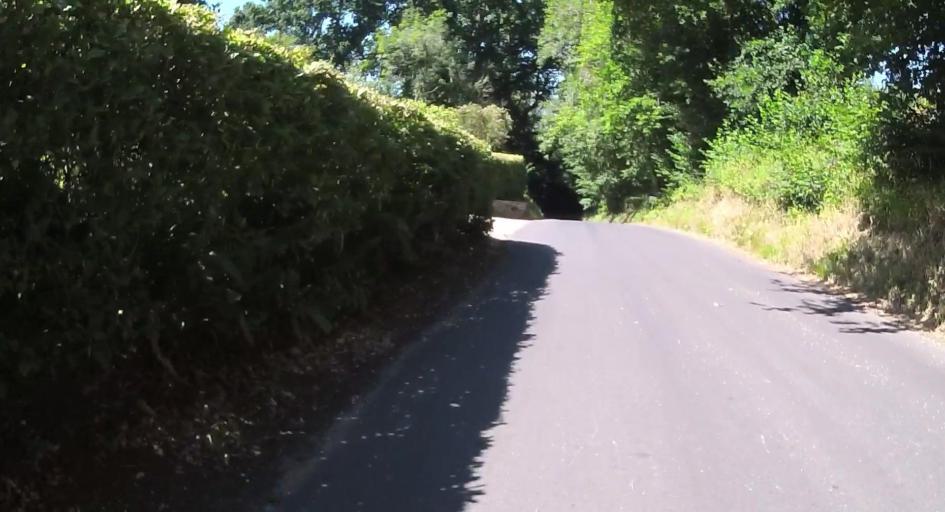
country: GB
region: England
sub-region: Dorset
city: Bovington Camp
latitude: 50.7361
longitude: -2.2619
